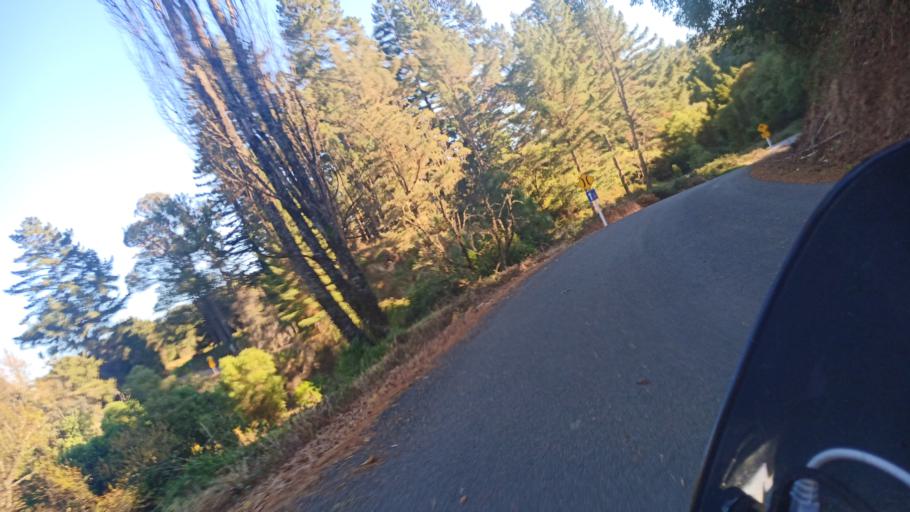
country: NZ
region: Hawke's Bay
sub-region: Wairoa District
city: Wairoa
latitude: -38.8166
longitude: 177.2949
